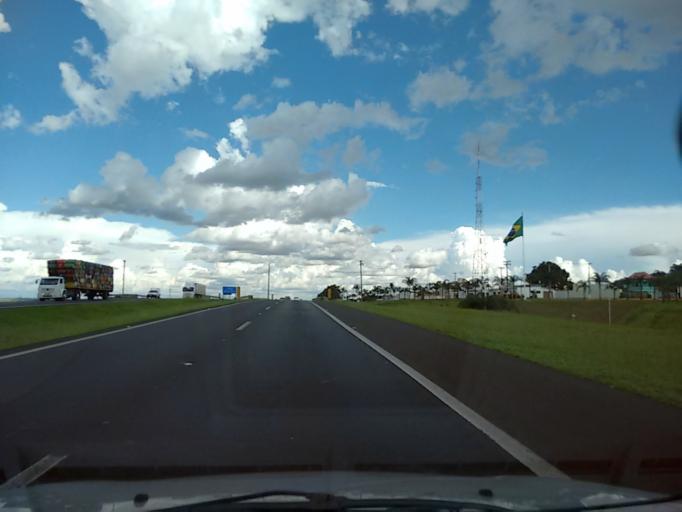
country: BR
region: Sao Paulo
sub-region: Ibate
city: Ibate
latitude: -21.9501
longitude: -47.9938
